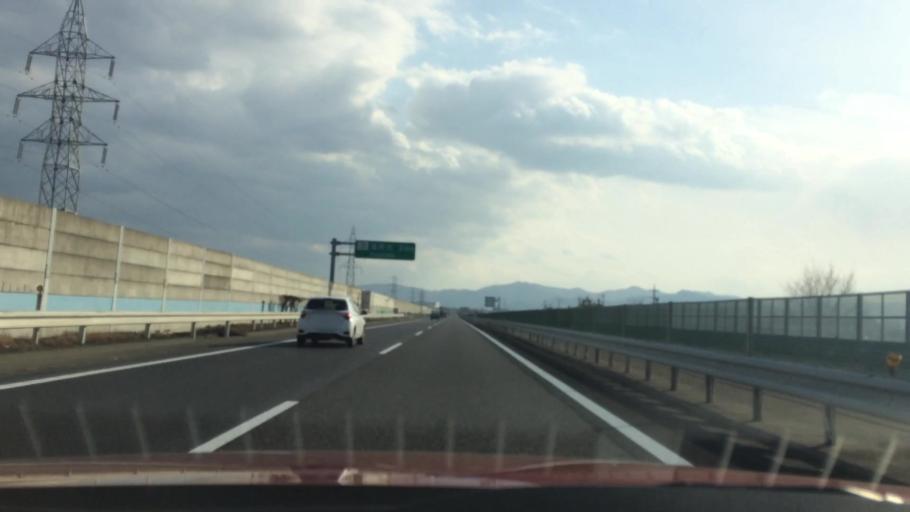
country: JP
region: Nagano
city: Matsumoto
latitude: 36.1855
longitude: 137.9385
